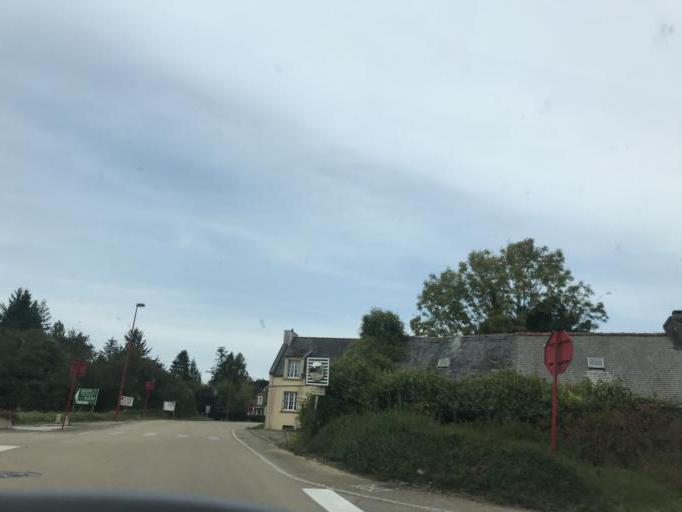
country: FR
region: Brittany
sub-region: Departement du Finistere
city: Plouneour-Menez
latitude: 48.3631
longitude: -3.8501
